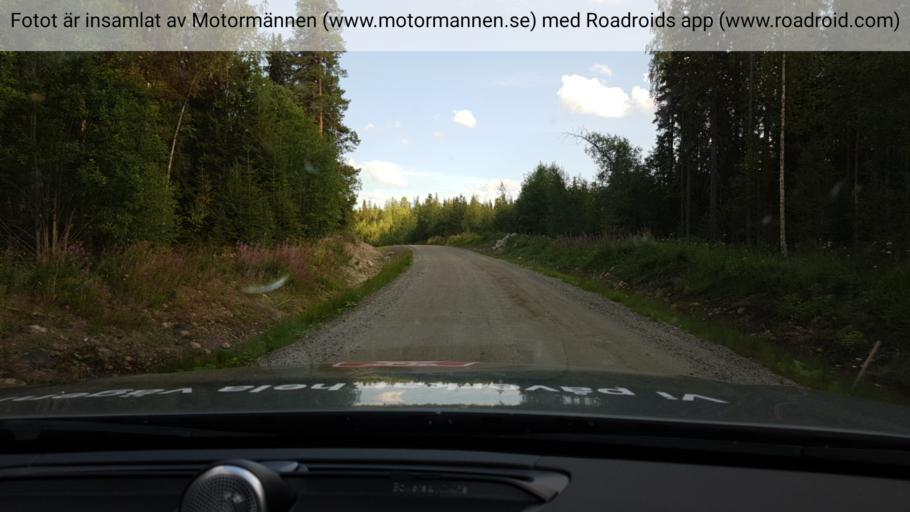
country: SE
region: Vaesterbotten
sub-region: Dorotea Kommun
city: Dorotea
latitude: 63.9225
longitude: 16.1787
